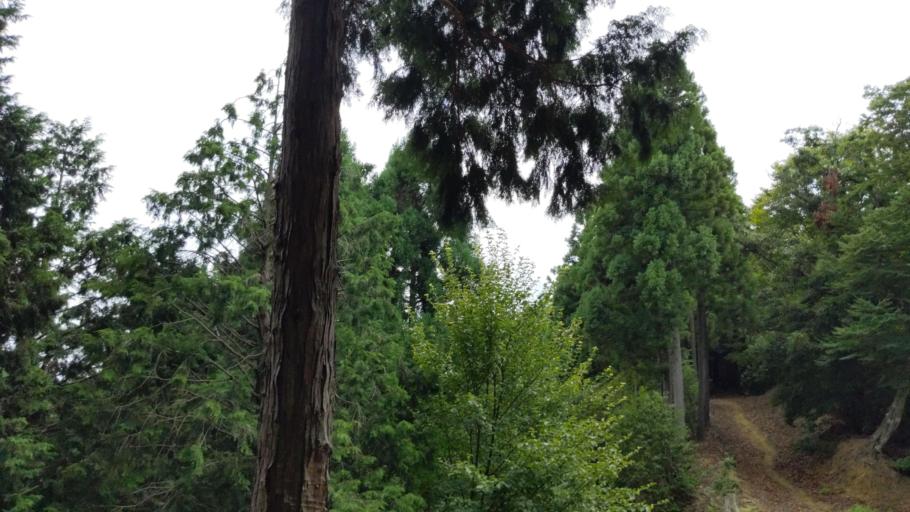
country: JP
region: Kyoto
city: Maizuru
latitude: 35.3958
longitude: 135.4409
